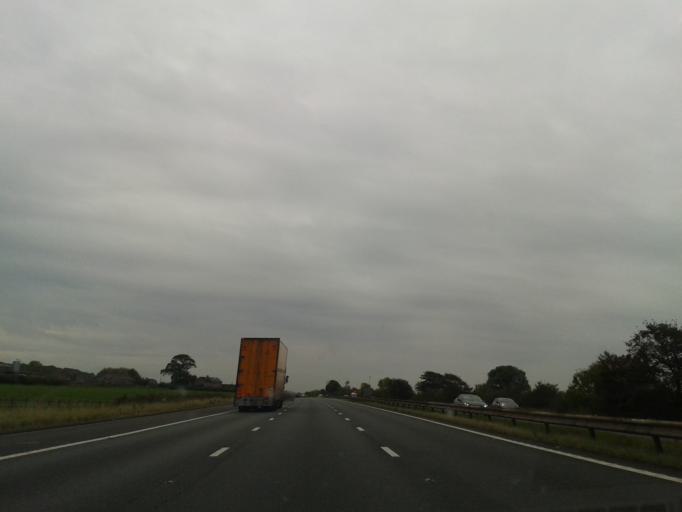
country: GB
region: England
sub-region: Cumbria
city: Milnthorpe
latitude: 54.2113
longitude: -2.7232
